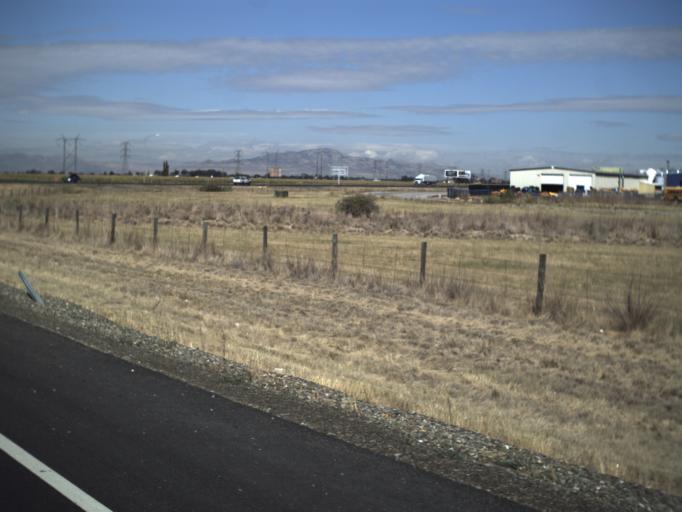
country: US
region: Utah
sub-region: Box Elder County
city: Brigham City
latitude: 41.5382
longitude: -112.0652
